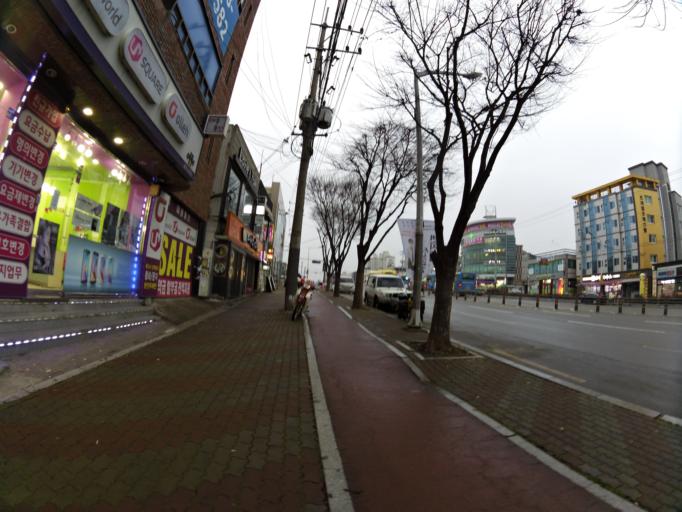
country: KR
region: Gyeongsangbuk-do
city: Gyeongsan-si
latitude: 35.8393
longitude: 128.7569
